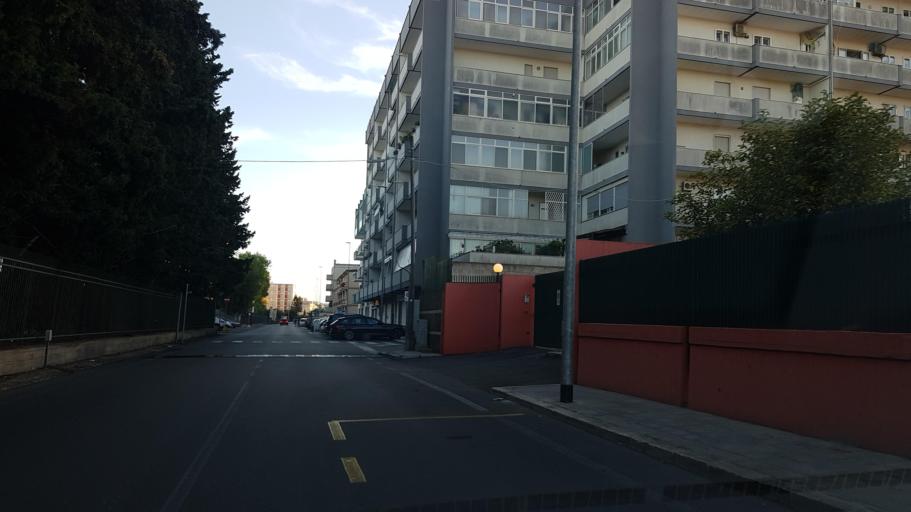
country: IT
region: Apulia
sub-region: Provincia di Lecce
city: Lecce
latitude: 40.3674
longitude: 18.1769
